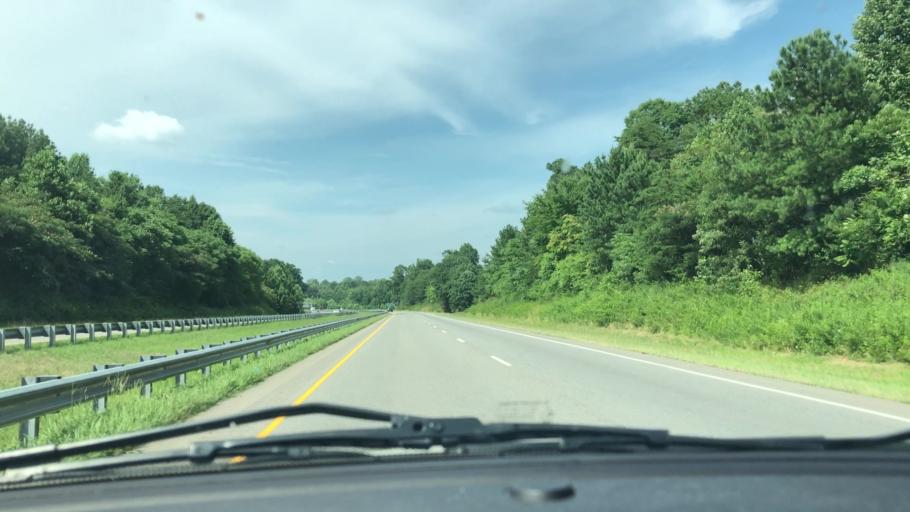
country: US
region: North Carolina
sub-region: Rockingham County
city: Stoneville
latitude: 36.5113
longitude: -79.9186
